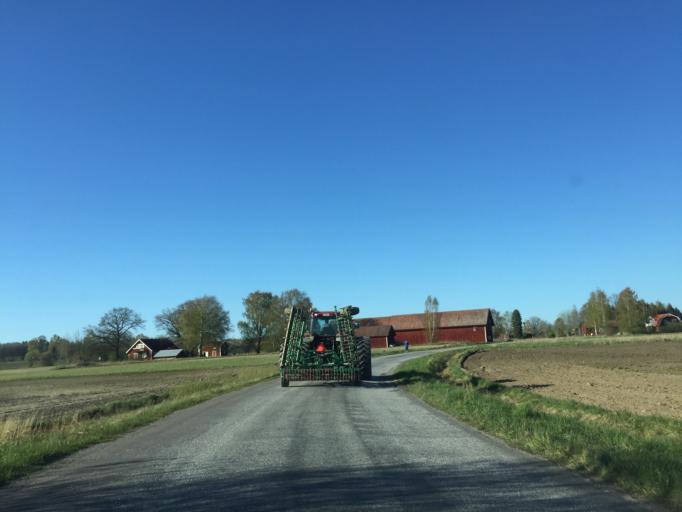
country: SE
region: OErebro
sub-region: Orebro Kommun
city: Odensbacken
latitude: 59.2069
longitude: 15.5499
